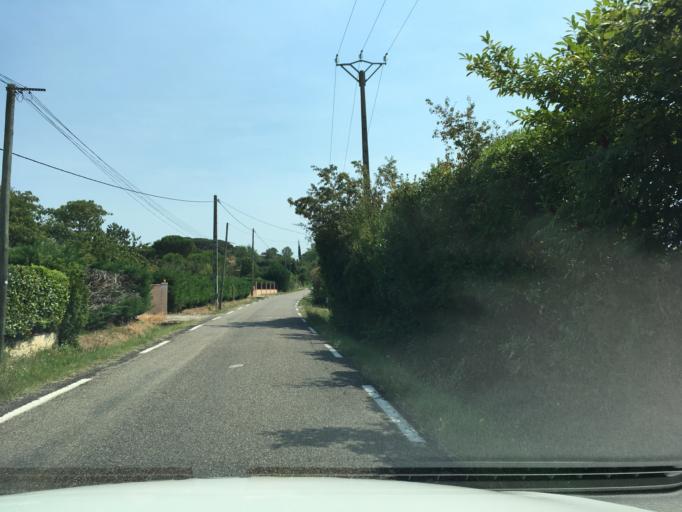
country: FR
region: Midi-Pyrenees
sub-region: Departement du Tarn-et-Garonne
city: Corbarieu
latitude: 43.9714
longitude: 1.3819
